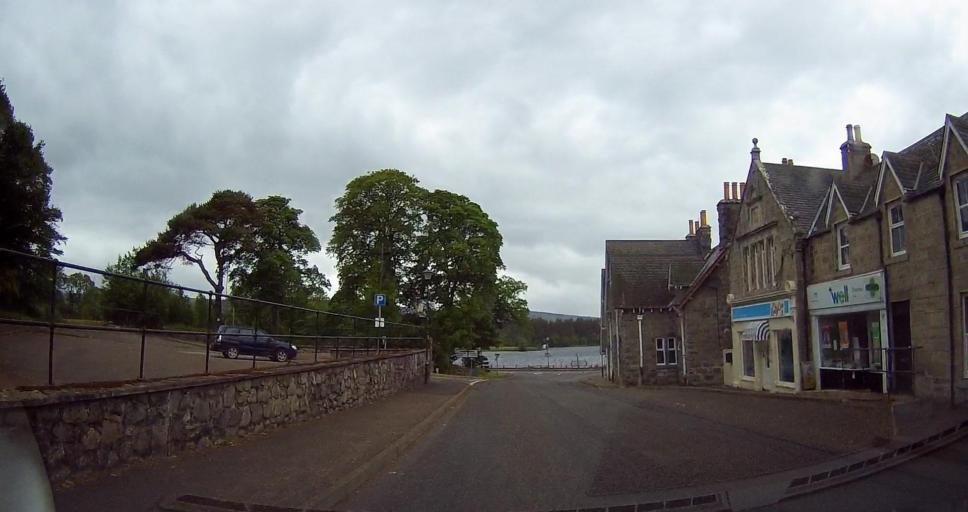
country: GB
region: Scotland
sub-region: Highland
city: Alness
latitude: 58.0240
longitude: -4.4002
